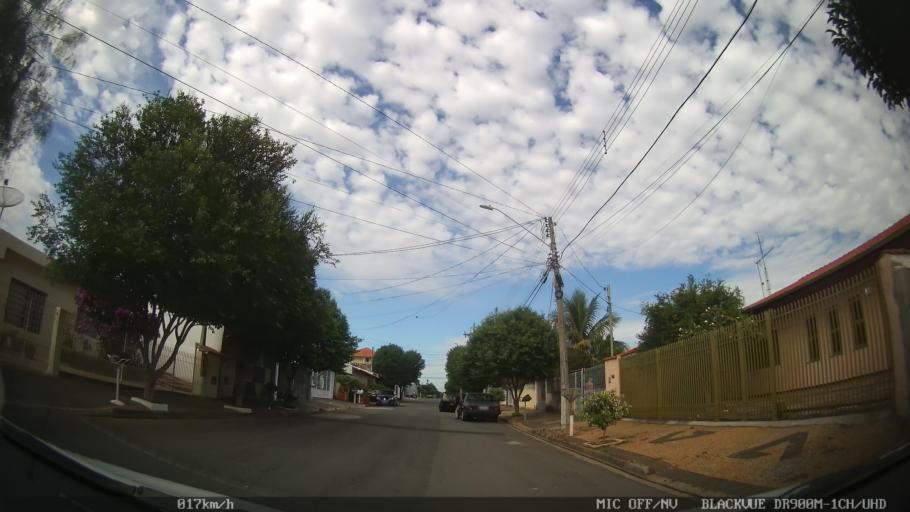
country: BR
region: Sao Paulo
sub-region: Americana
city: Americana
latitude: -22.7195
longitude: -47.3604
